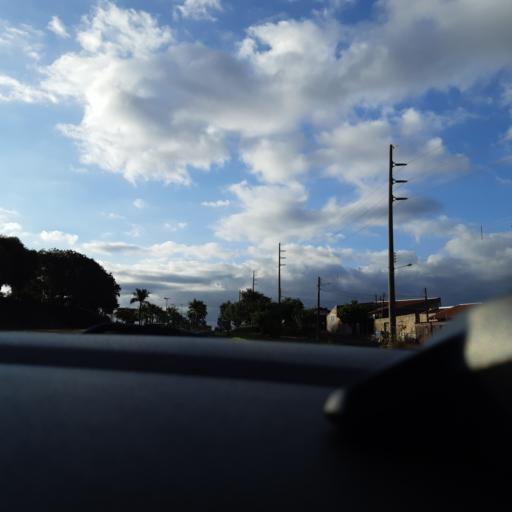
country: BR
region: Sao Paulo
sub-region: Ourinhos
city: Ourinhos
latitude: -22.9873
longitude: -49.8551
